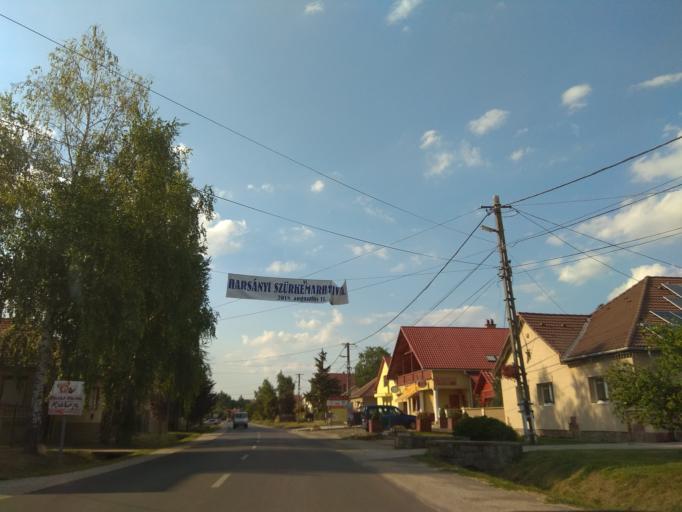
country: HU
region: Borsod-Abauj-Zemplen
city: Harsany
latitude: 47.9655
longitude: 20.7424
